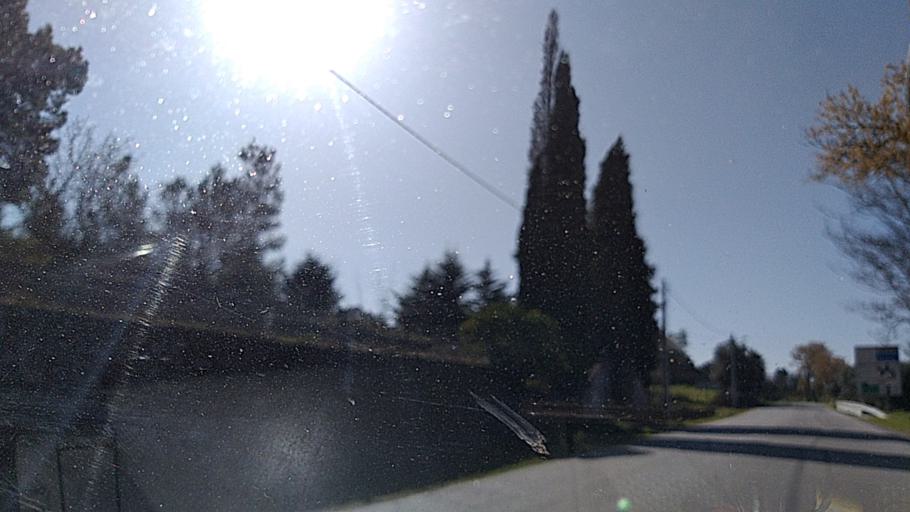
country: PT
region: Guarda
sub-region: Celorico da Beira
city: Celorico da Beira
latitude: 40.6612
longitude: -7.3820
